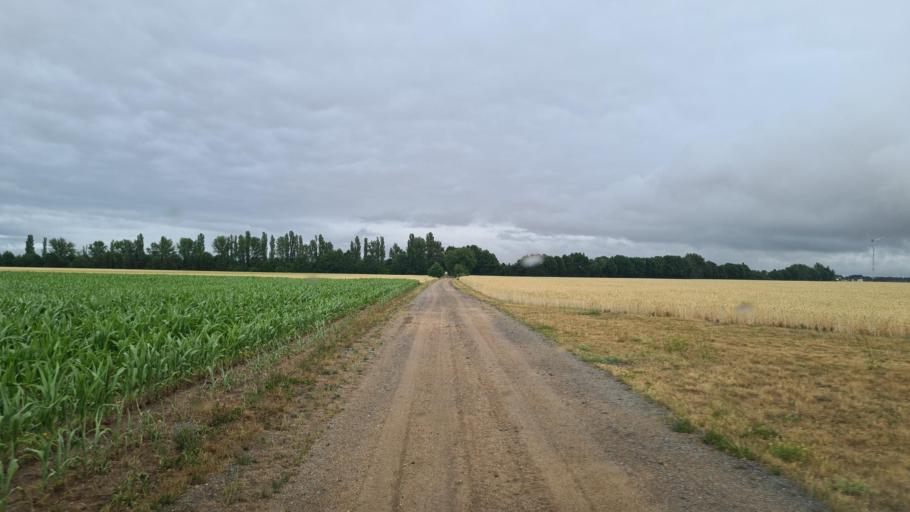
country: DE
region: Brandenburg
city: Bad Liebenwerda
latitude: 51.4959
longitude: 13.3238
